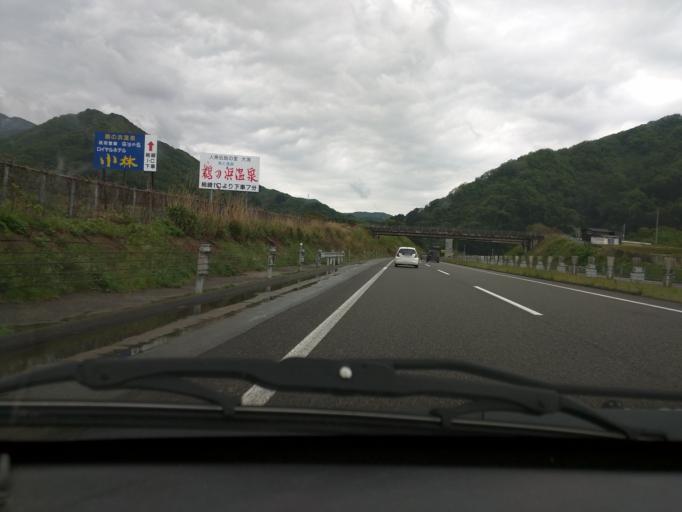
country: JP
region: Niigata
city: Kashiwazaki
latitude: 37.3267
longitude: 138.4600
